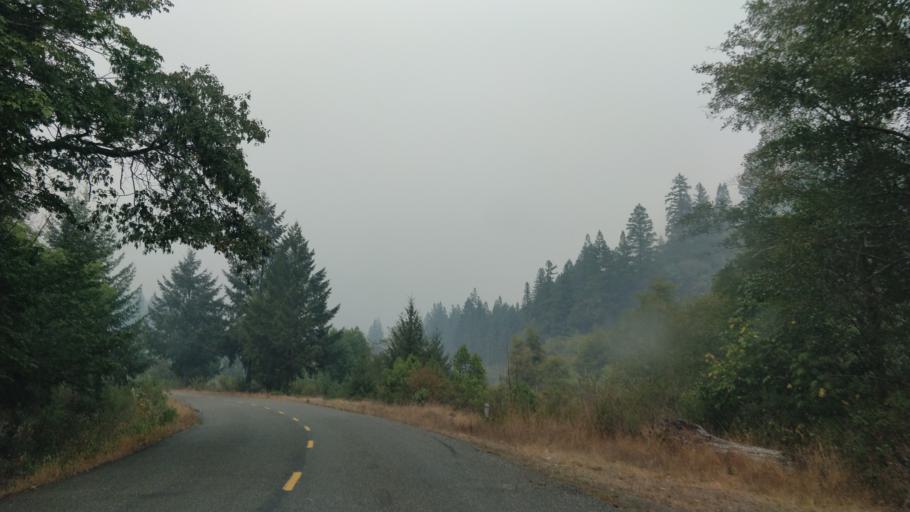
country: US
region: California
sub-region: Humboldt County
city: Rio Dell
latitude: 40.3400
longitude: -124.0266
